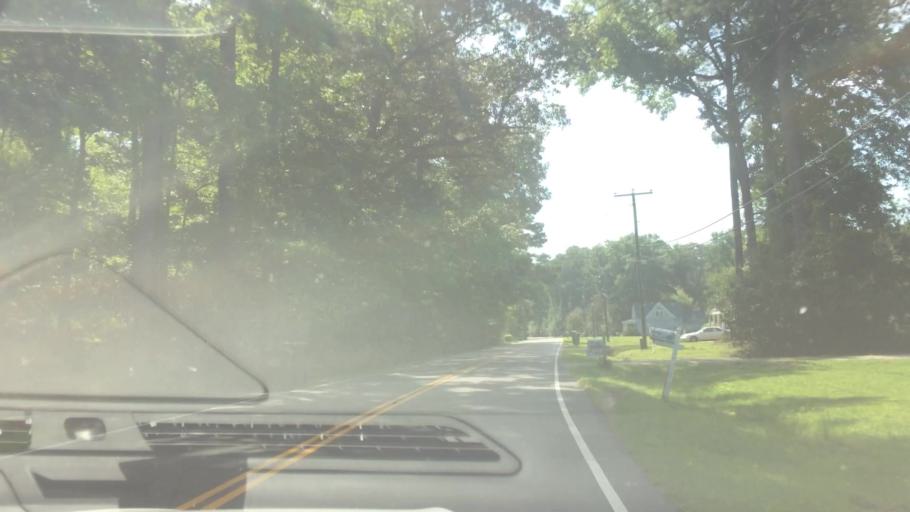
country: US
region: Virginia
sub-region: City of Poquoson
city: Poquoson
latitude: 37.1671
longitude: -76.4314
